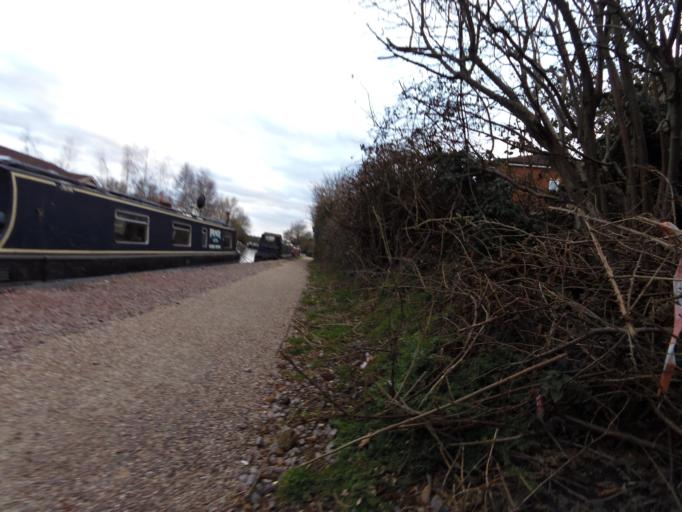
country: GB
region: England
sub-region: Hertfordshire
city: Rickmansworth
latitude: 51.6462
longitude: -0.4376
